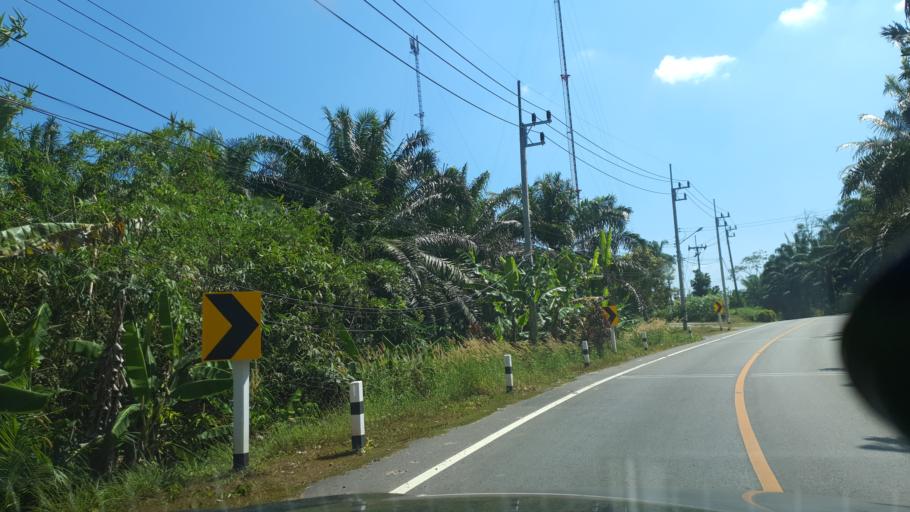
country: TH
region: Krabi
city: Khlong Thom
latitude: 7.9251
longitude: 99.2431
